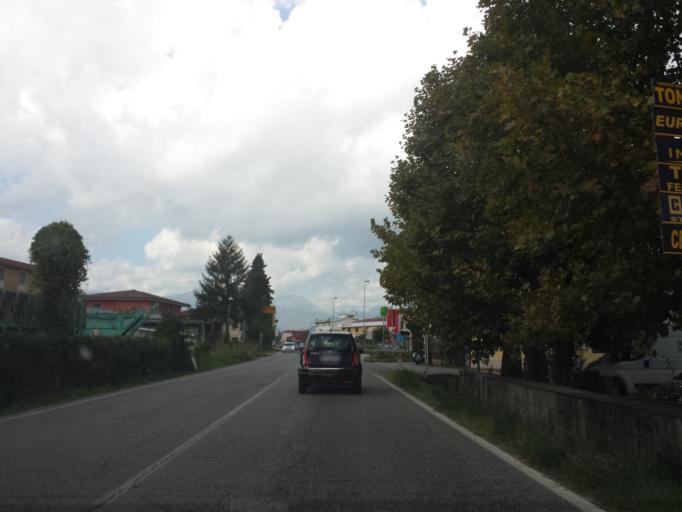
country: IT
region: Veneto
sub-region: Provincia di Vicenza
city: Cereda-Cozza Cornedo
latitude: 45.5966
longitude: 11.3702
